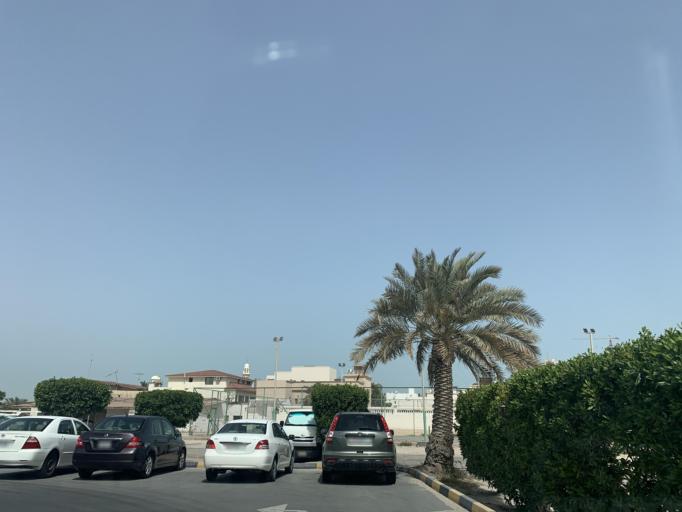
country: BH
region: Manama
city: Jidd Hafs
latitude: 26.2158
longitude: 50.5607
